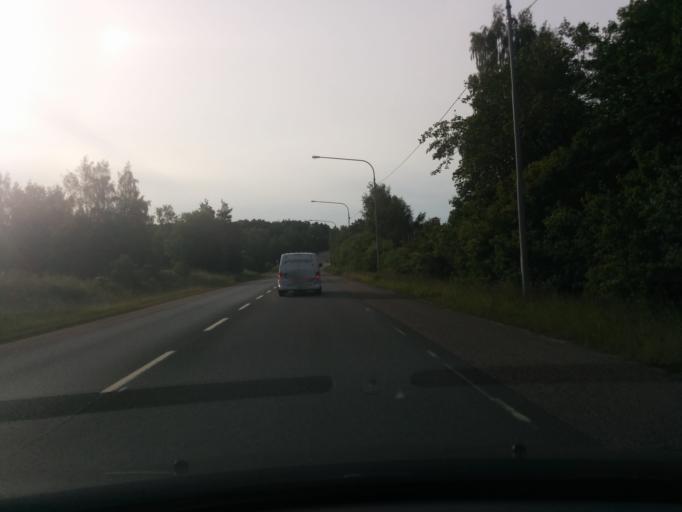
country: SE
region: Stockholm
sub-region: Norrtalje Kommun
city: Bergshamra
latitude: 59.4139
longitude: 18.0217
